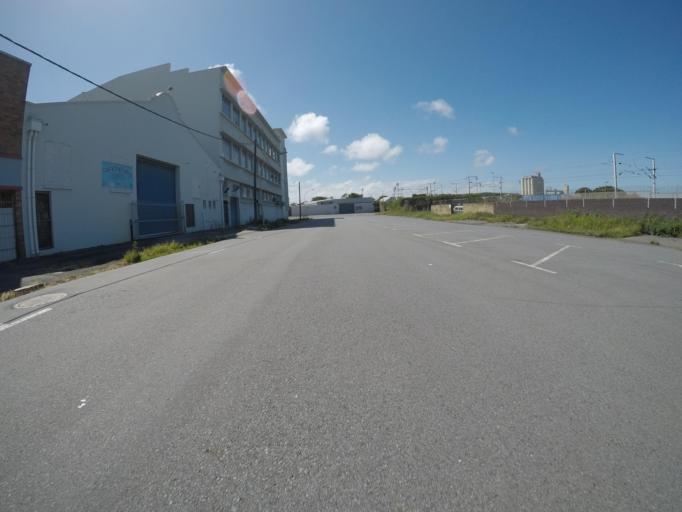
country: ZA
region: Eastern Cape
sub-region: Buffalo City Metropolitan Municipality
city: East London
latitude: -33.0139
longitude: 27.9061
